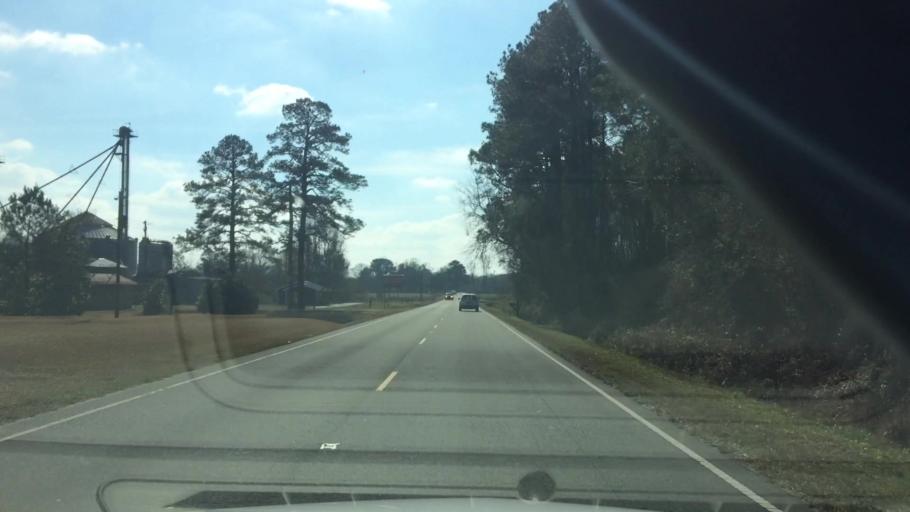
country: US
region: North Carolina
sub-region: Duplin County
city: Beulaville
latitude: 34.8612
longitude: -77.7956
